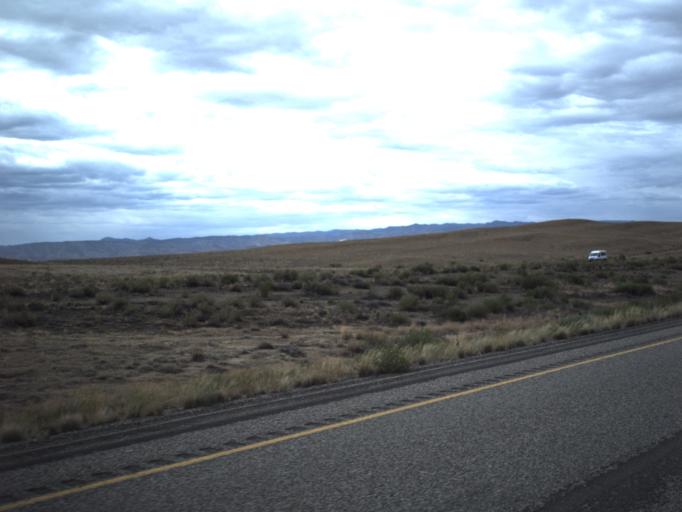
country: US
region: Colorado
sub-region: Mesa County
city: Loma
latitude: 39.1449
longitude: -109.1517
